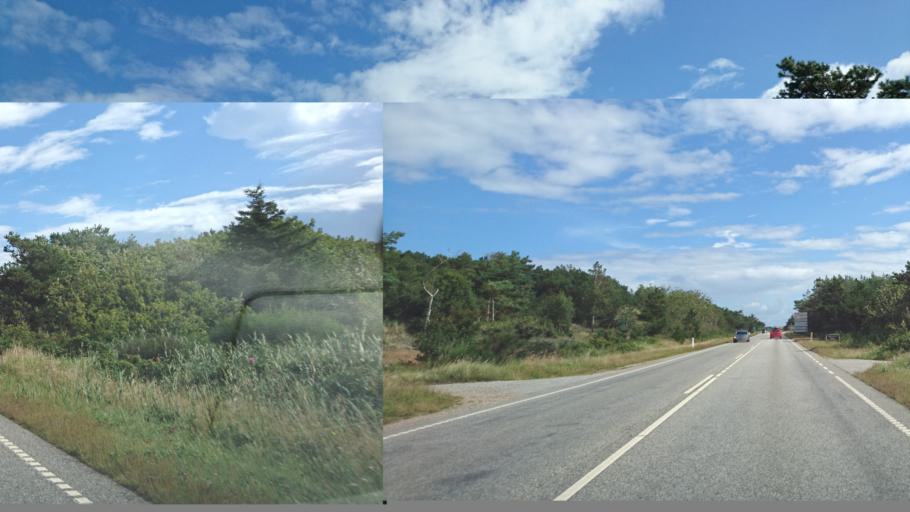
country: DK
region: North Denmark
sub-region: Frederikshavn Kommune
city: Skagen
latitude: 57.7178
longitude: 10.5335
